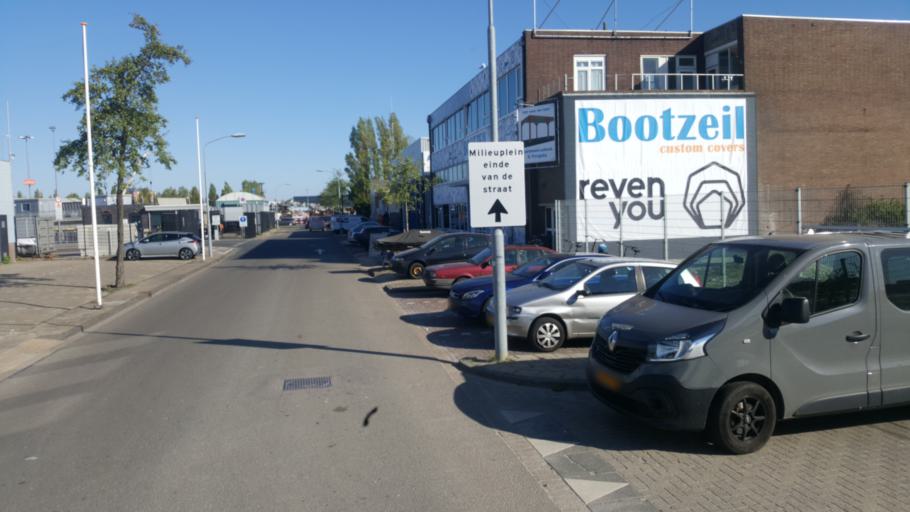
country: NL
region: North Holland
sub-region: Gemeente Haarlem
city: Haarlem
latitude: 52.3874
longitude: 4.6563
